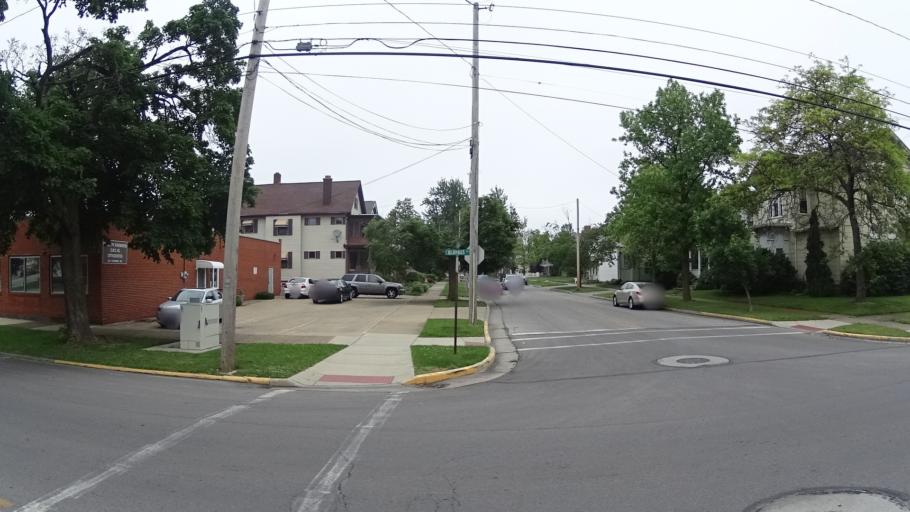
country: US
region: Ohio
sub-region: Erie County
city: Sandusky
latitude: 41.4515
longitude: -82.7090
